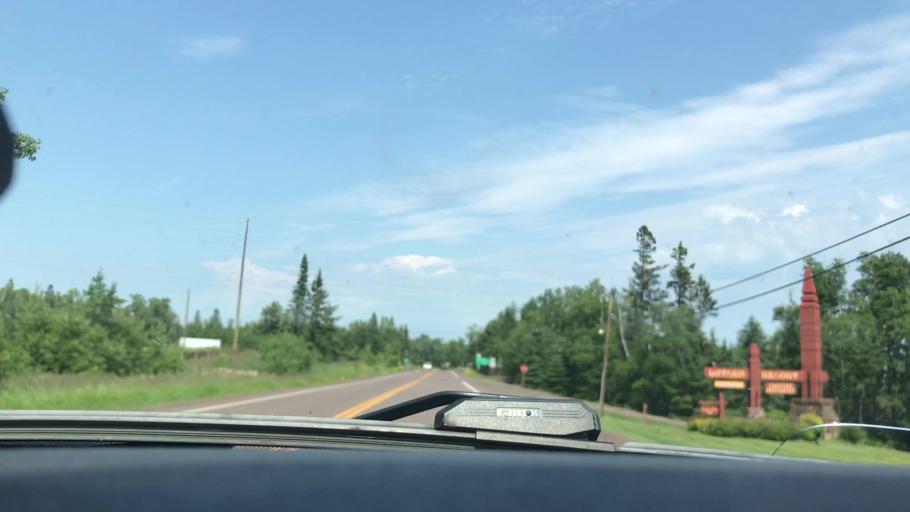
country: US
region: Minnesota
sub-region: Cook County
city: Grand Marais
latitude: 47.6379
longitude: -90.7101
